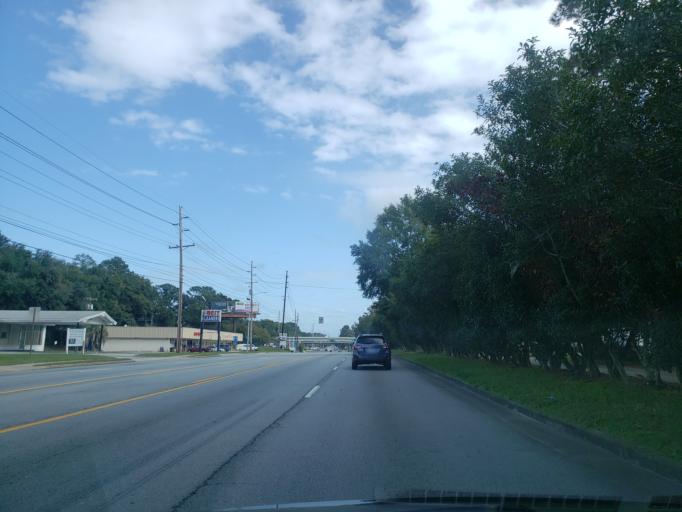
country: US
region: Georgia
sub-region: Chatham County
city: Thunderbolt
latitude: 32.0238
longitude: -81.0920
